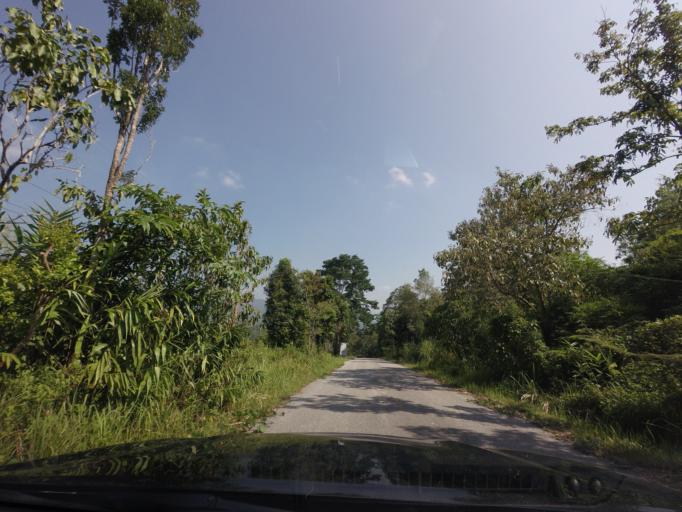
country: TH
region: Loei
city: Na Haeo
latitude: 17.5340
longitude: 101.0032
